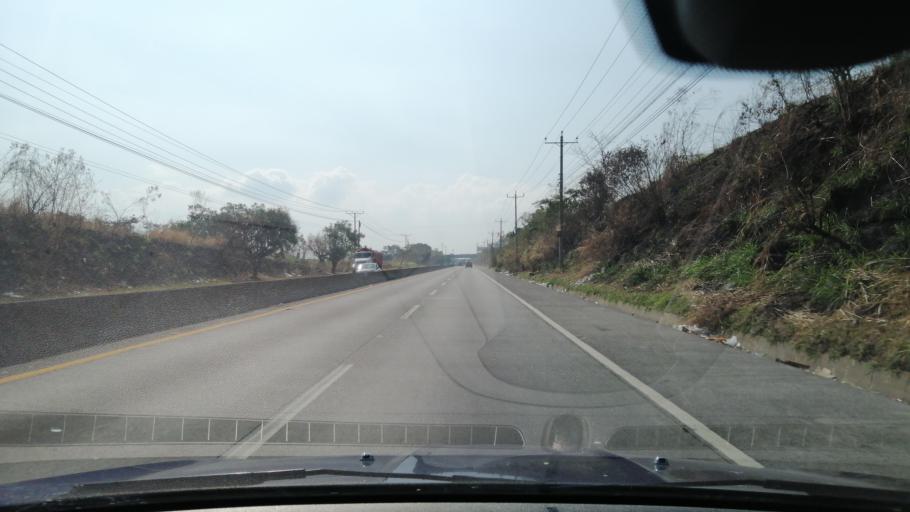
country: SV
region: San Salvador
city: Apopa
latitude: 13.7903
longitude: -89.2214
